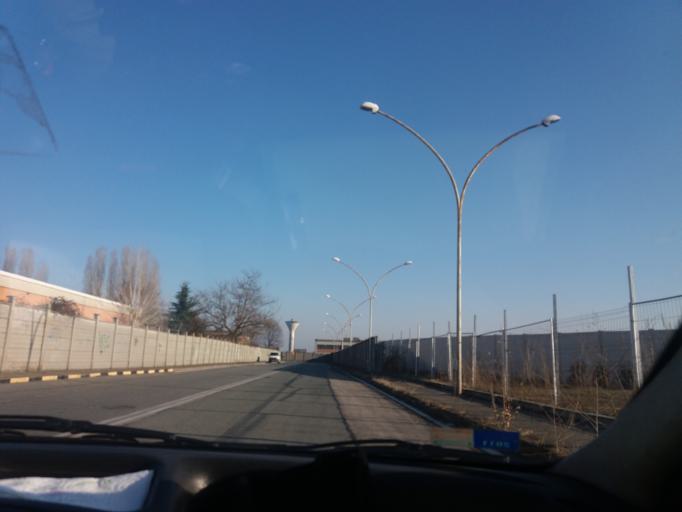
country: IT
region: Piedmont
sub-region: Provincia di Torino
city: Fornaci
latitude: 45.0282
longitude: 7.6093
